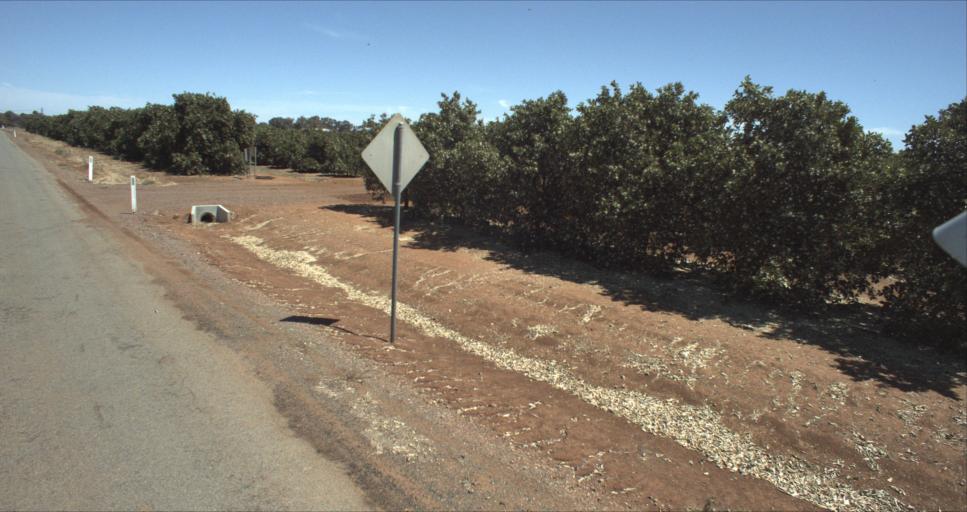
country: AU
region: New South Wales
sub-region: Leeton
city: Leeton
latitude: -34.5320
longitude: 146.3288
